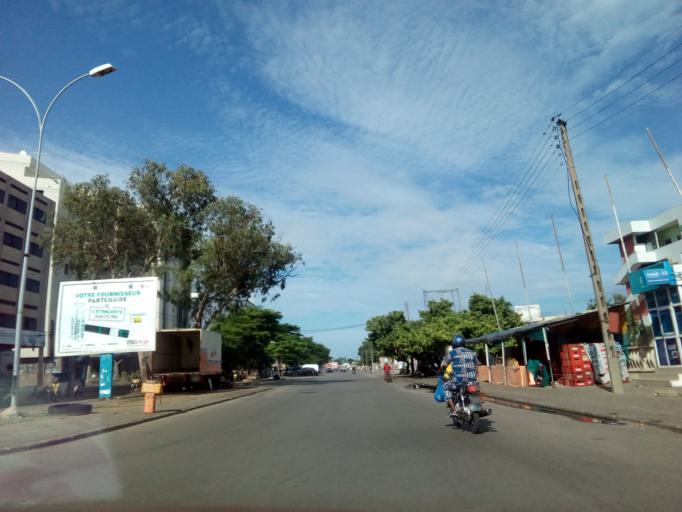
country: BJ
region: Littoral
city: Cotonou
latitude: 6.3600
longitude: 2.4208
